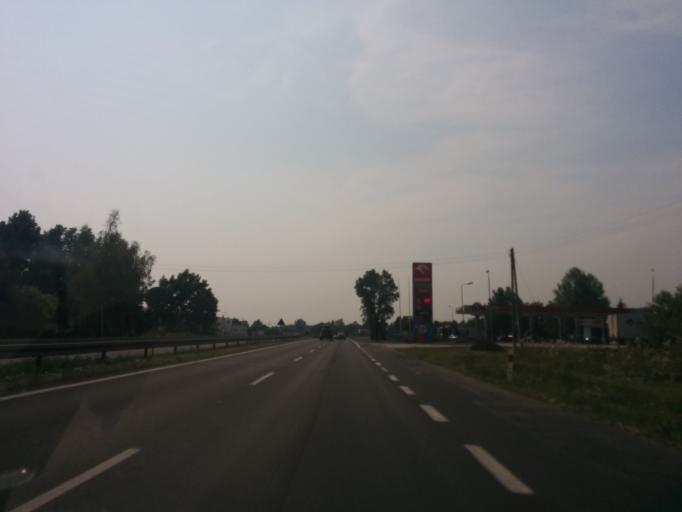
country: PL
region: Lodz Voivodeship
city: Zabia Wola
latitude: 52.0404
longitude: 20.6991
